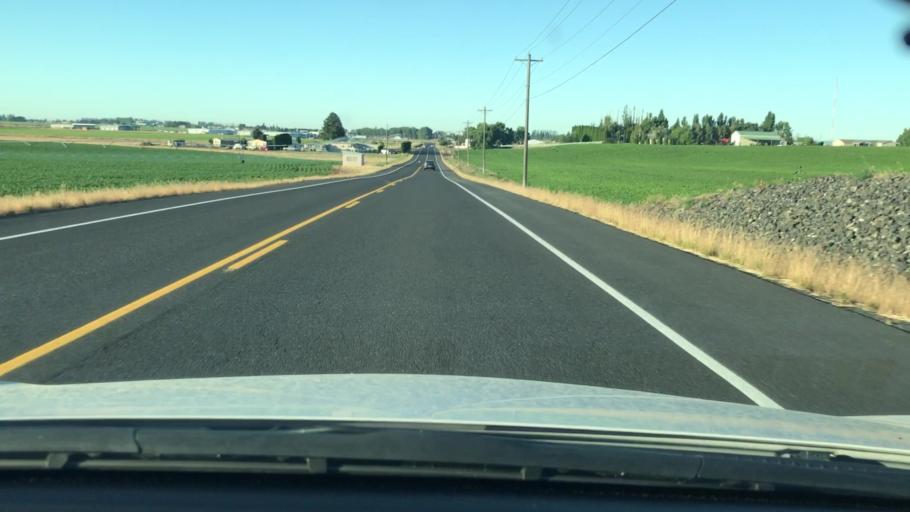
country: US
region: Washington
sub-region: Grant County
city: Moses Lake
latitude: 47.1089
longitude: -119.2383
